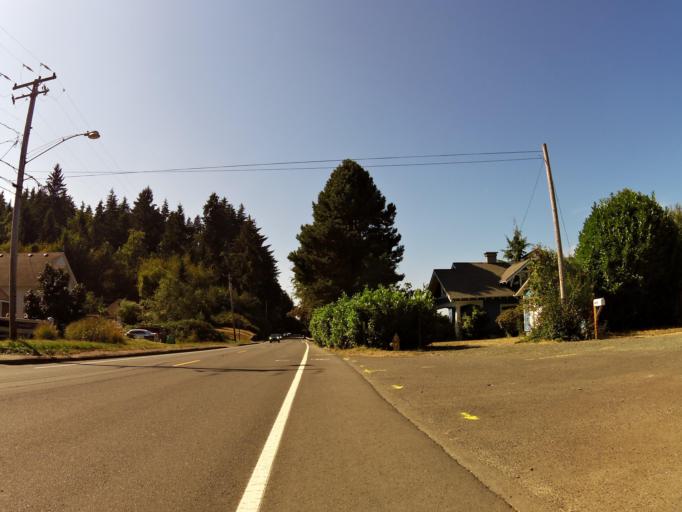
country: US
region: Oregon
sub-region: Clatsop County
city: Astoria
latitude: 46.1943
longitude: -123.7824
